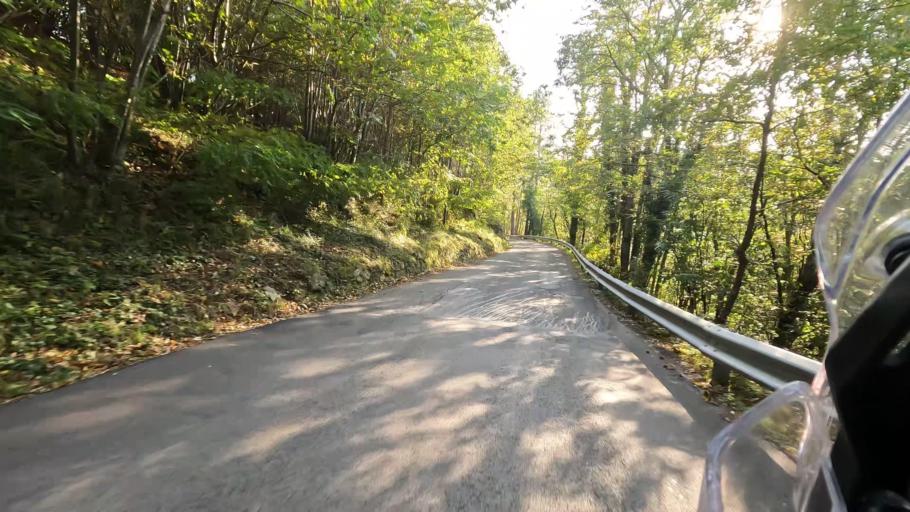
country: IT
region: Liguria
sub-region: Provincia di Savona
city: San Giovanni
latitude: 44.4118
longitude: 8.5194
